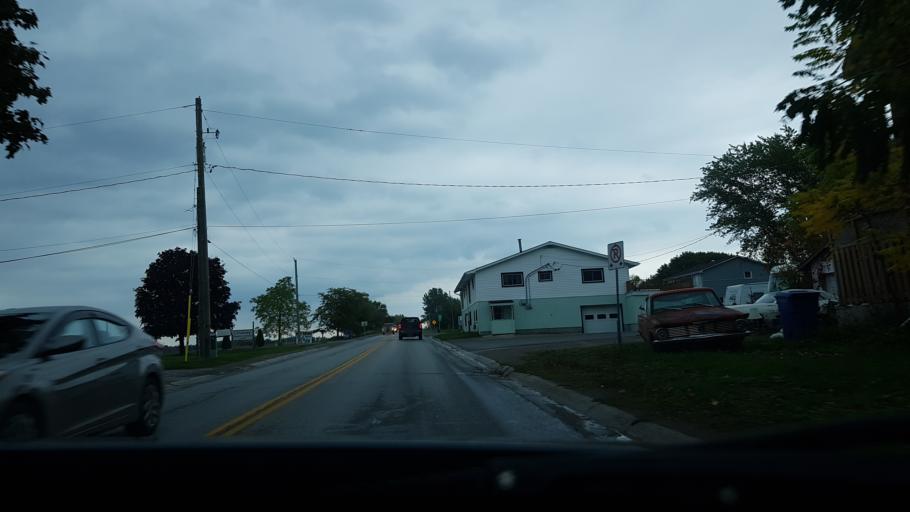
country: CA
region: Ontario
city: Omemee
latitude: 44.3616
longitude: -78.7189
